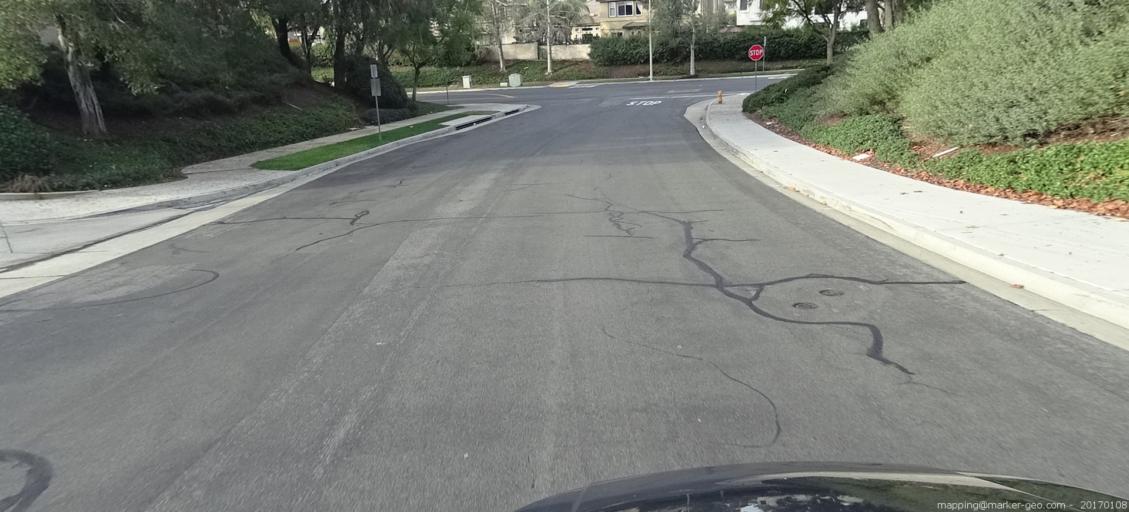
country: US
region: California
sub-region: Orange County
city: Las Flores
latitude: 33.5883
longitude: -117.6238
